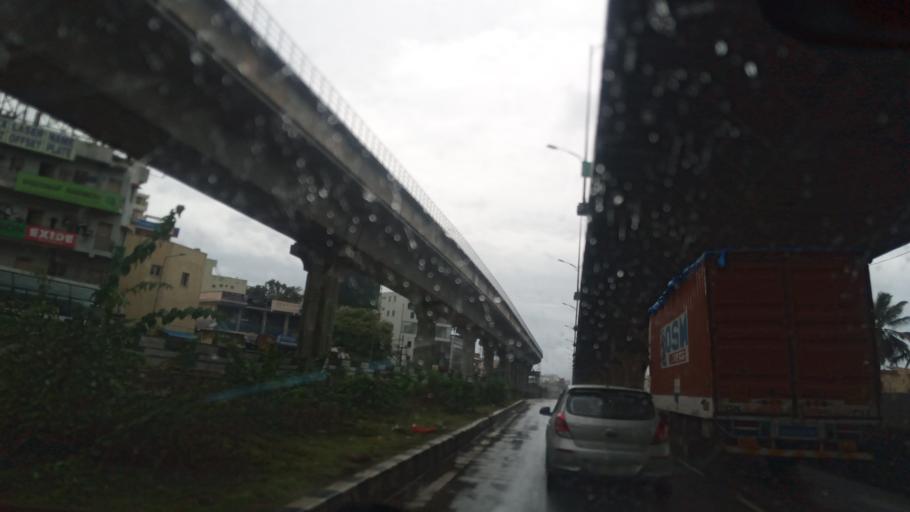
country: IN
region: Karnataka
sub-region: Bangalore Urban
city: Bangalore
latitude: 12.8537
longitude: 77.6653
